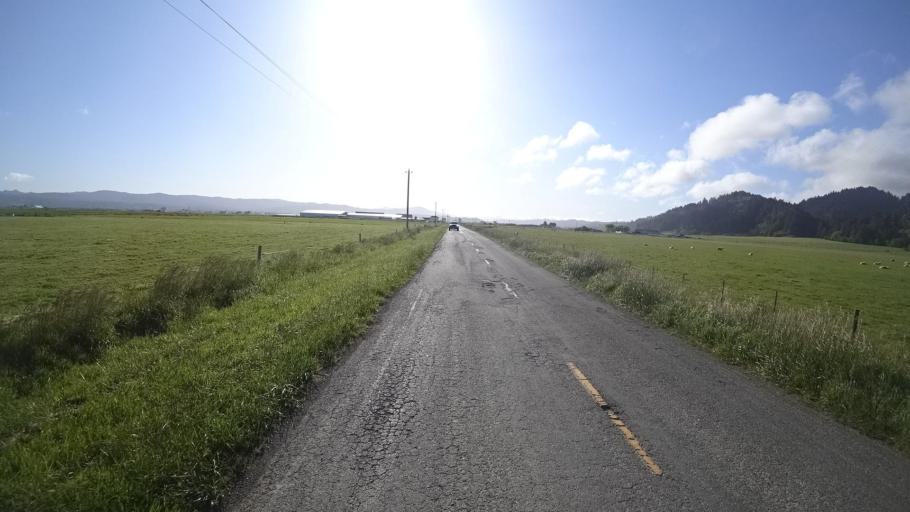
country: US
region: California
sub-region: Humboldt County
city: Ferndale
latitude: 40.5719
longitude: -124.2276
